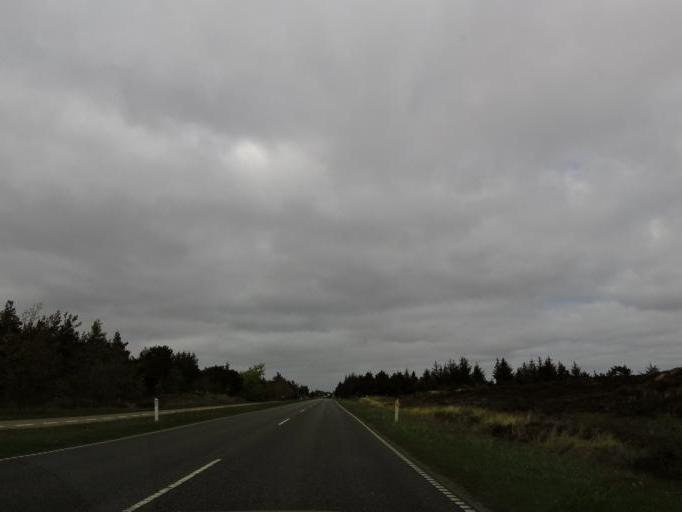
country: DE
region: Schleswig-Holstein
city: List
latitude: 55.1218
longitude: 8.5479
